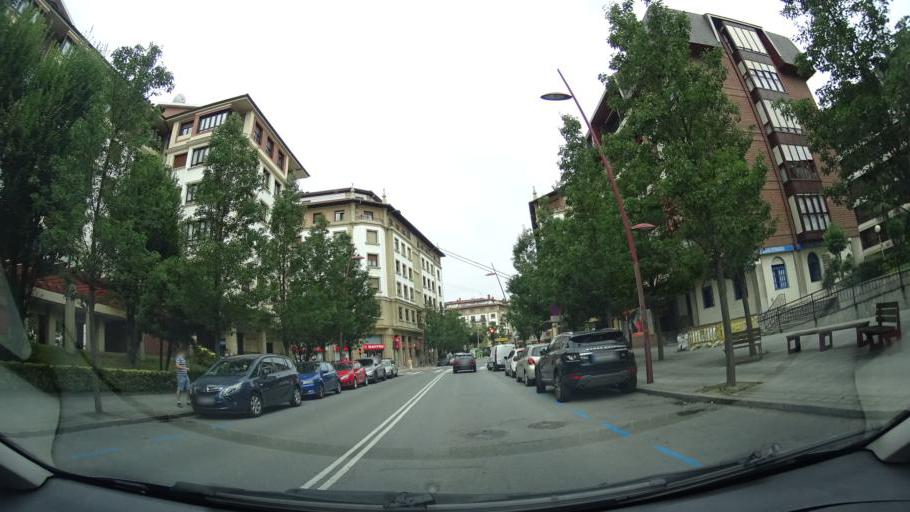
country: ES
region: Basque Country
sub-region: Bizkaia
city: Portugalete
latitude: 43.3230
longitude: -3.0149
